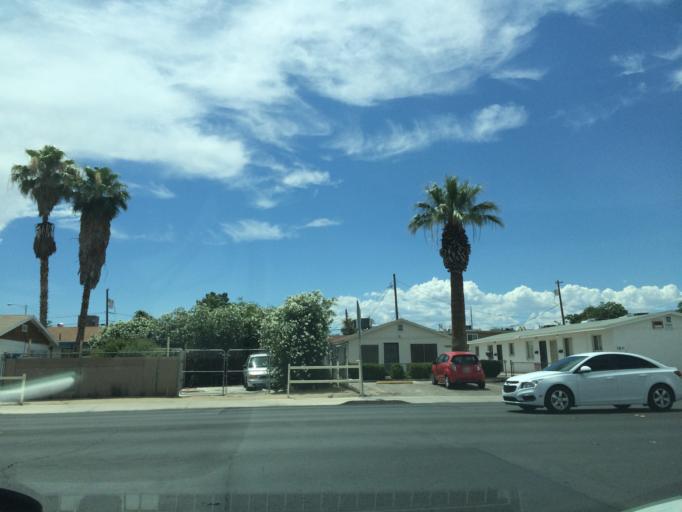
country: US
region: Nevada
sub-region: Clark County
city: North Las Vegas
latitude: 36.1944
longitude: -115.1249
